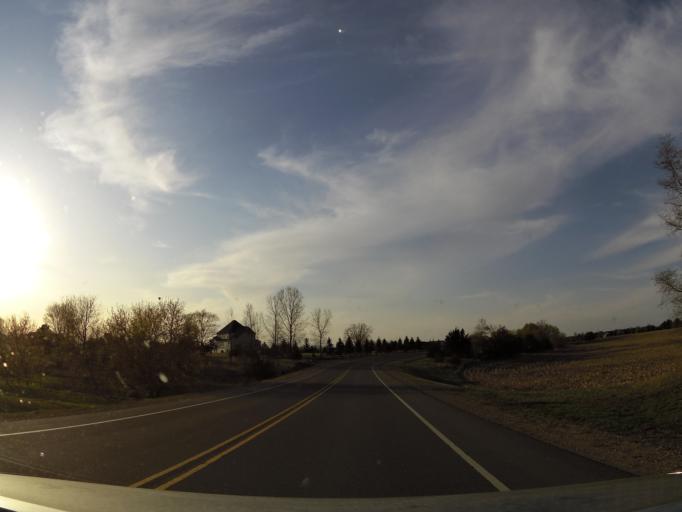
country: US
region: Minnesota
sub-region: Washington County
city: Lake Saint Croix Beach
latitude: 44.9272
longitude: -92.6969
